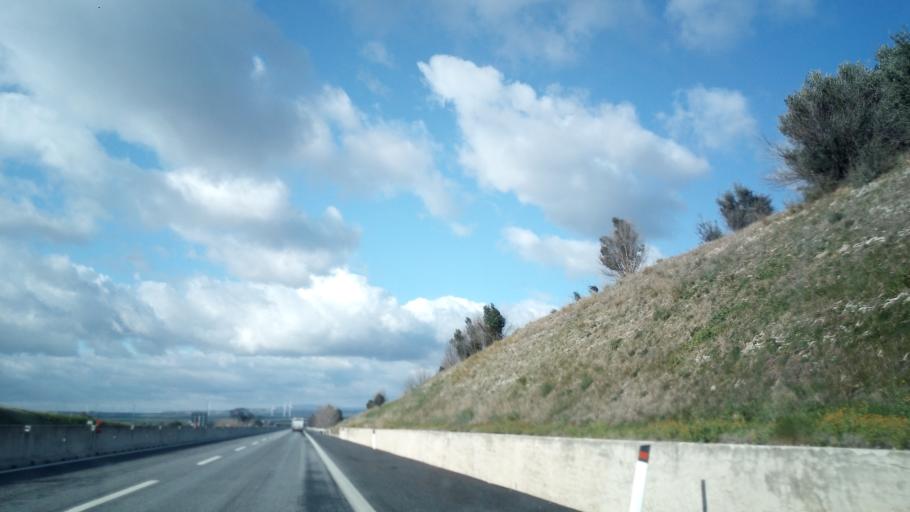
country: IT
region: Apulia
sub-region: Provincia di Foggia
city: Stornarella
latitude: 41.1794
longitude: 15.7164
